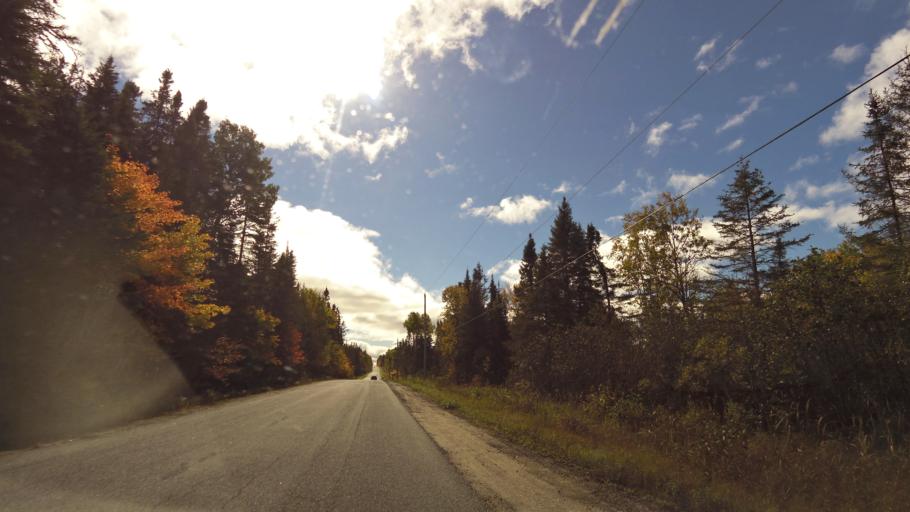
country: CA
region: Ontario
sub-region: Nipissing District
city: North Bay
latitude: 46.3672
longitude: -79.4872
